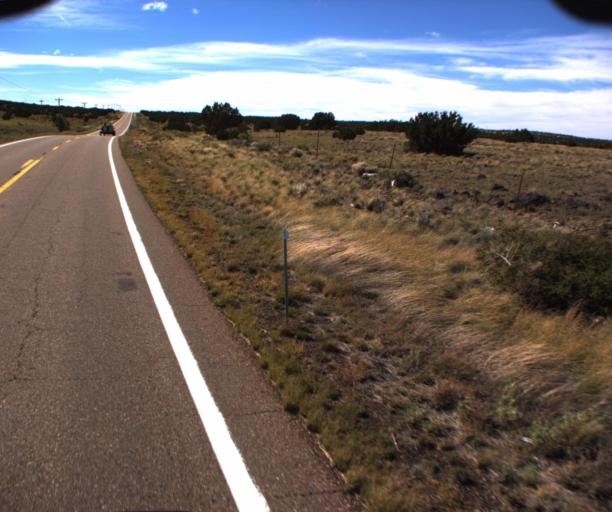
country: US
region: Arizona
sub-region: Apache County
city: Saint Johns
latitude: 34.4857
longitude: -109.5398
